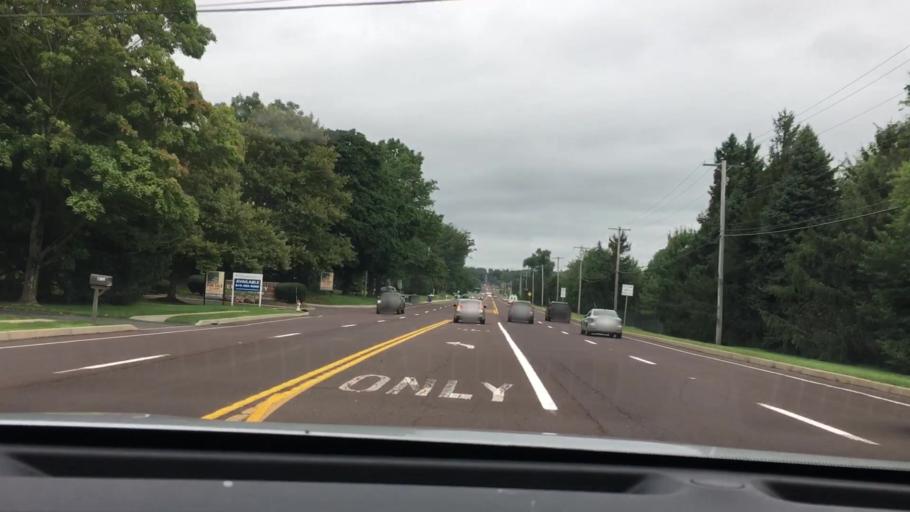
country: US
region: Pennsylvania
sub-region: Montgomery County
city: Maple Glen
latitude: 40.1954
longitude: -75.1578
